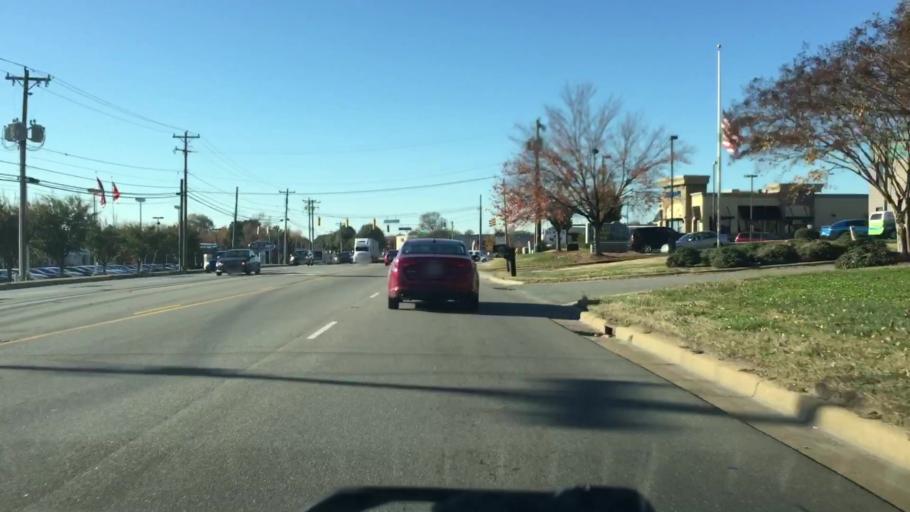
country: US
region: North Carolina
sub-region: Iredell County
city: Mooresville
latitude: 35.5919
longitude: -80.8495
